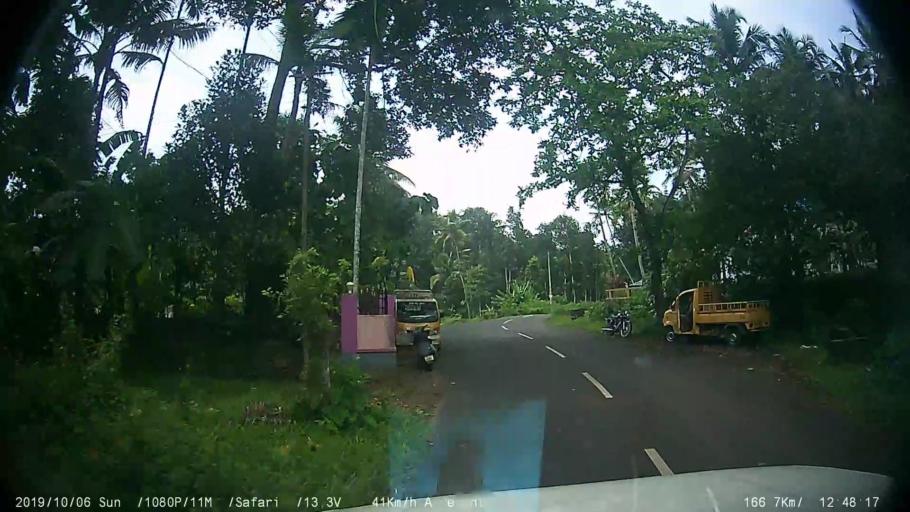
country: IN
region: Kerala
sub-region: Kottayam
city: Palackattumala
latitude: 9.7783
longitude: 76.5978
